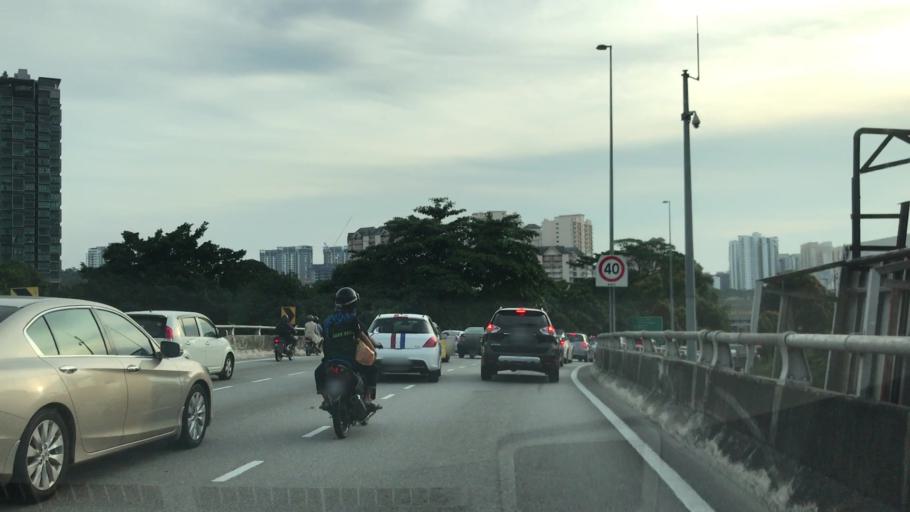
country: MY
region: Kuala Lumpur
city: Kuala Lumpur
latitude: 3.0880
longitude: 101.6970
